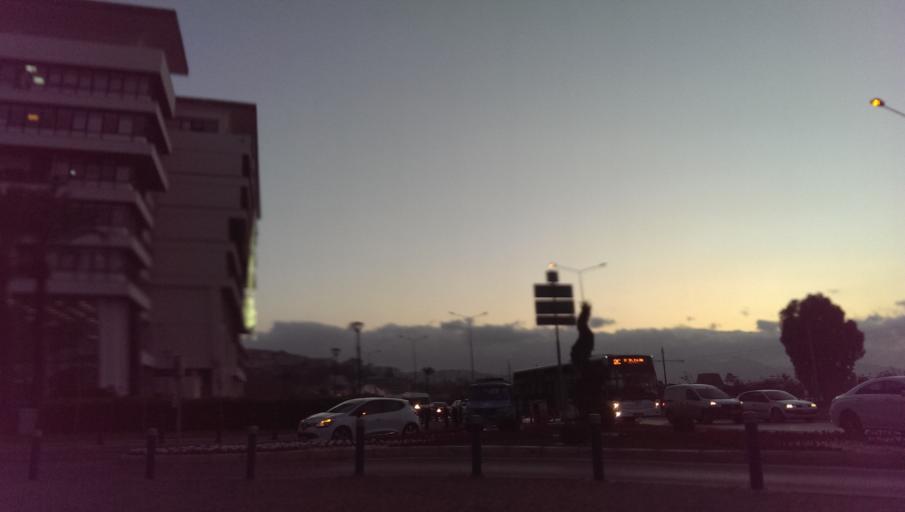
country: TR
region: Izmir
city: Izmir
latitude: 38.4206
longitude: 27.1289
